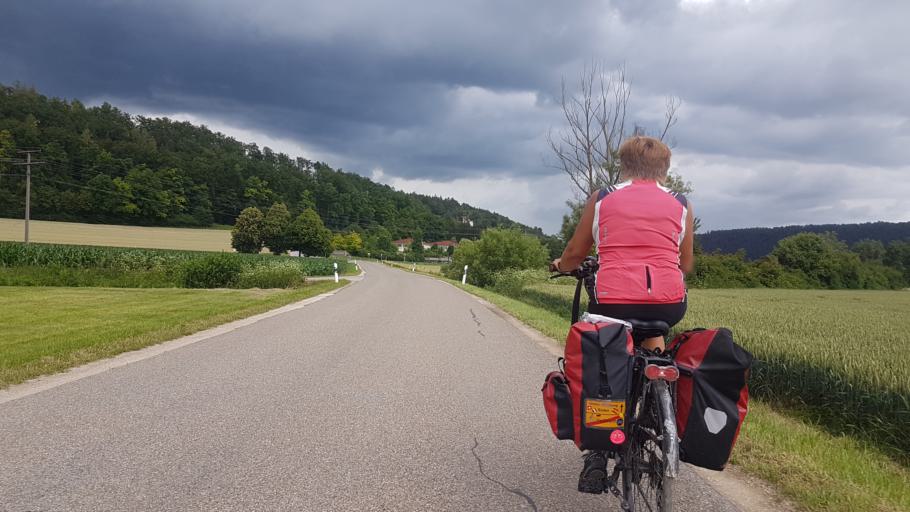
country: DE
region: Bavaria
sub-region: Upper Bavaria
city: Denkendorf
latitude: 48.9944
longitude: 11.4353
